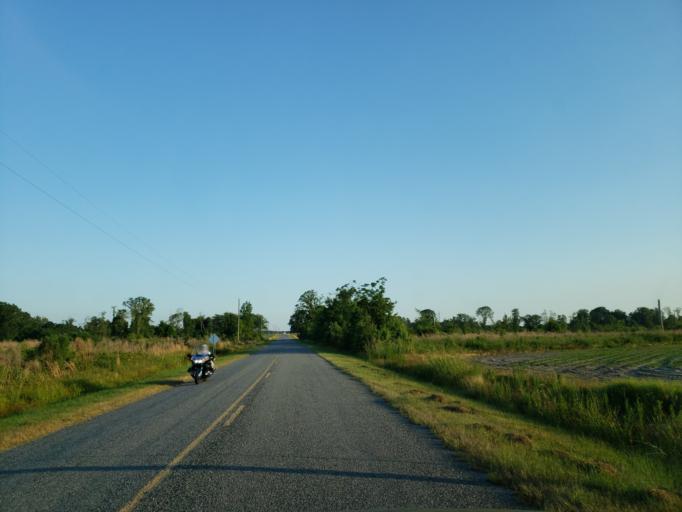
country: US
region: Georgia
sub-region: Dooly County
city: Vienna
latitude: 32.0996
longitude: -83.7564
